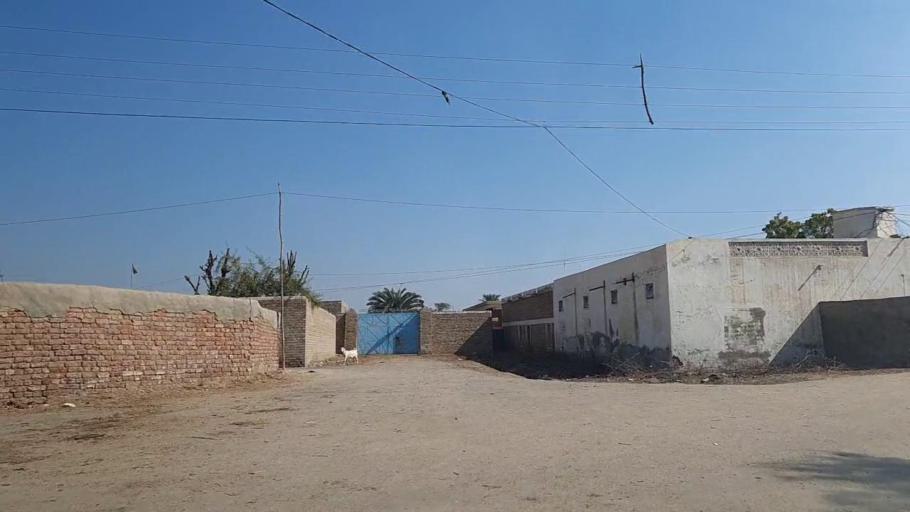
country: PK
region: Sindh
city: Nawabshah
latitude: 26.3484
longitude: 68.3797
